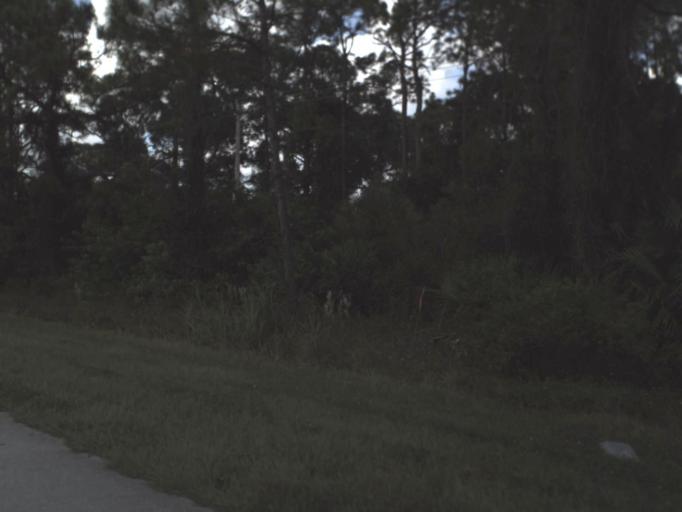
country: US
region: Florida
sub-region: Lee County
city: Lehigh Acres
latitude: 26.5121
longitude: -81.5386
